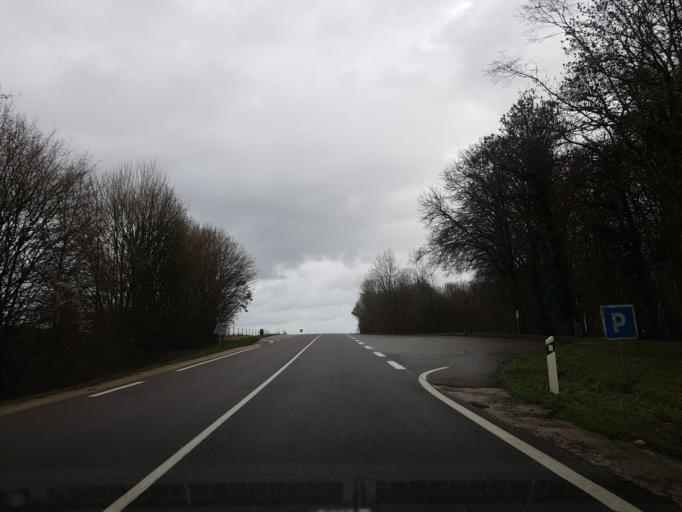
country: FR
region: Franche-Comte
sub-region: Departement de la Haute-Saone
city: Scey-sur-Saone-et-Saint-Albin
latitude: 47.7055
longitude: 5.9320
